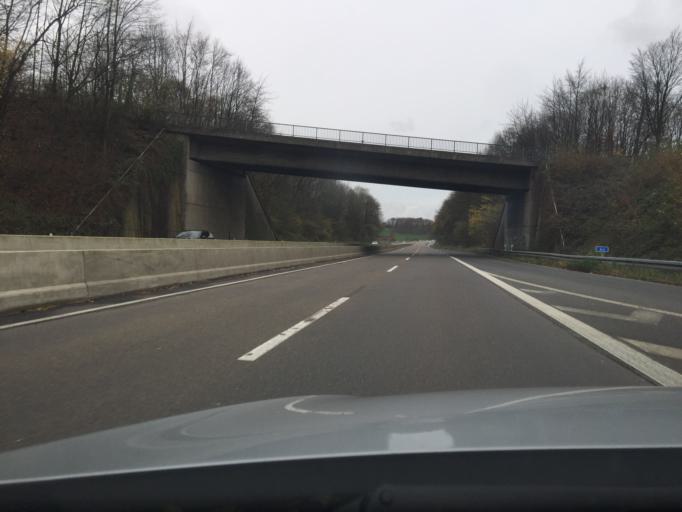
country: DE
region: North Rhine-Westphalia
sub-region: Regierungsbezirk Dusseldorf
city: Velbert
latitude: 51.3177
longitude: 7.0715
